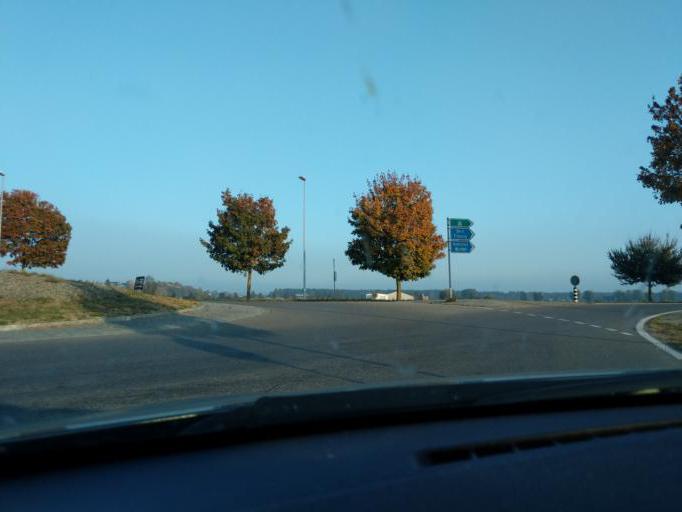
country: CH
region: Bern
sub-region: Seeland District
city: Ins
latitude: 46.9955
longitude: 7.1084
